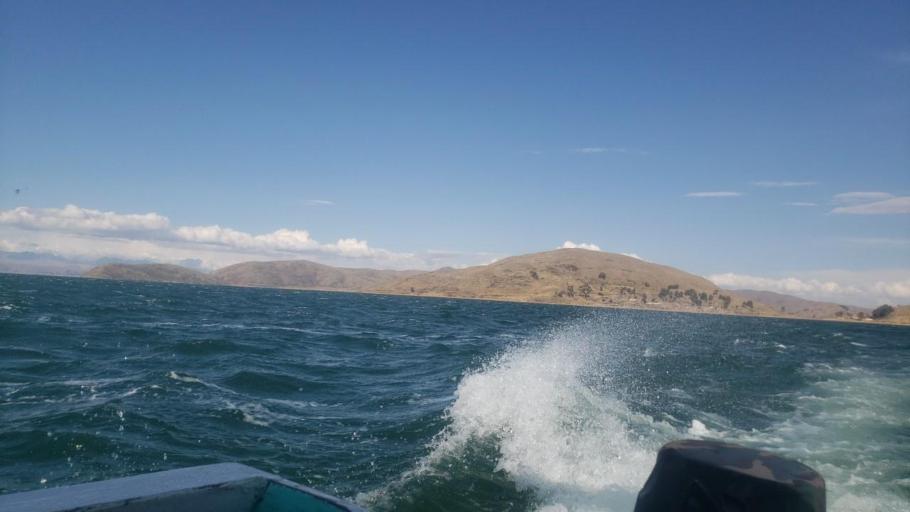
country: BO
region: La Paz
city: Huatajata
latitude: -16.3211
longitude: -68.7339
